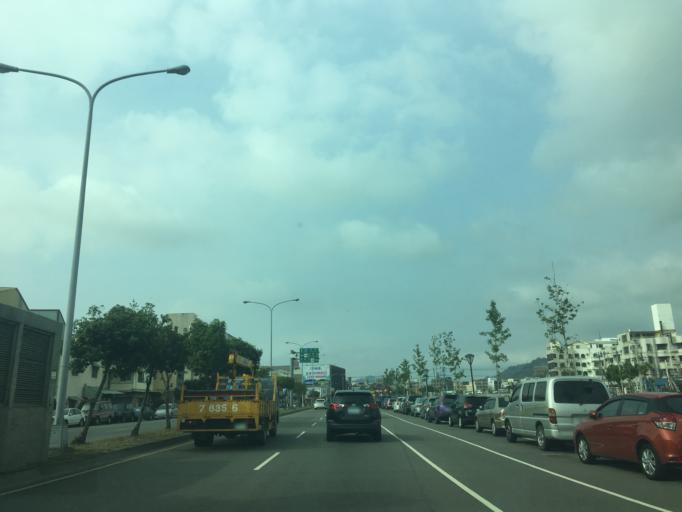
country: TW
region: Taiwan
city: Fengyuan
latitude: 24.2420
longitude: 120.7288
